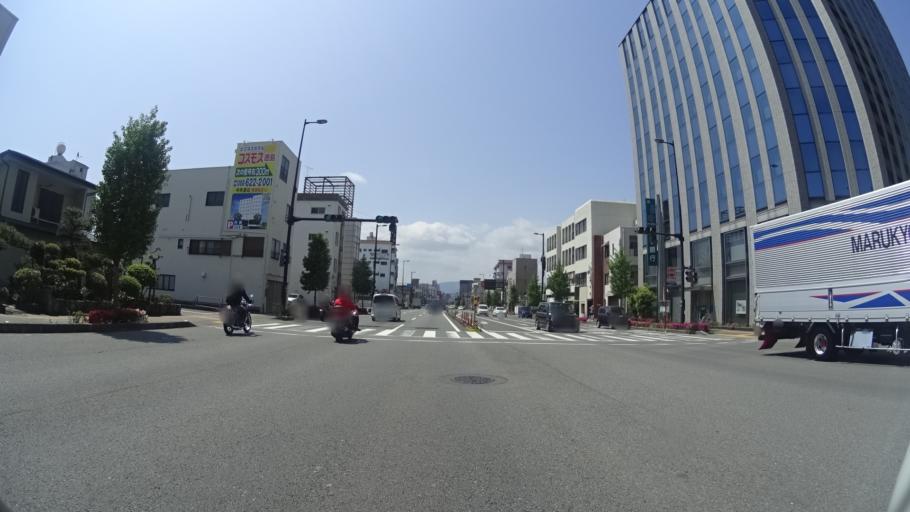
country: JP
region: Tokushima
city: Tokushima-shi
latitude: 34.0637
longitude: 134.5564
